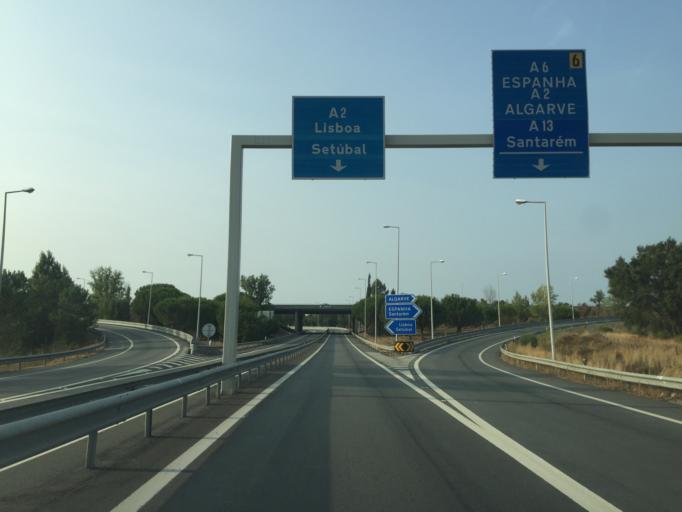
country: PT
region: Setubal
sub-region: Setubal
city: Setubal
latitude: 38.5995
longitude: -8.6738
